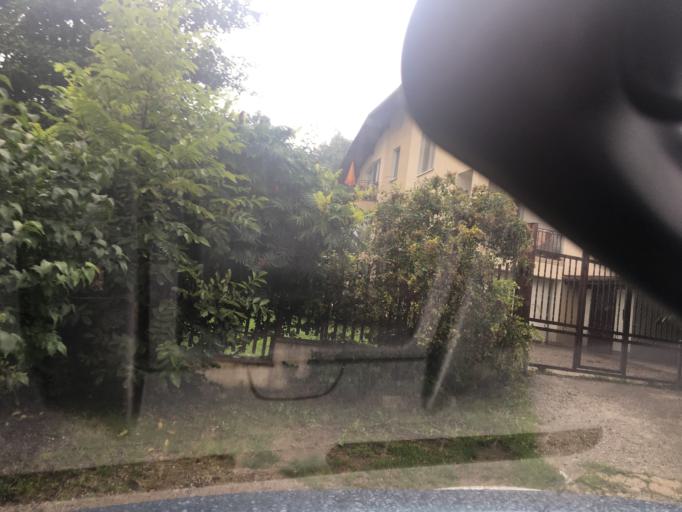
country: BG
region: Sofia-Capital
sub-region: Stolichna Obshtina
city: Sofia
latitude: 42.5837
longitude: 23.3501
